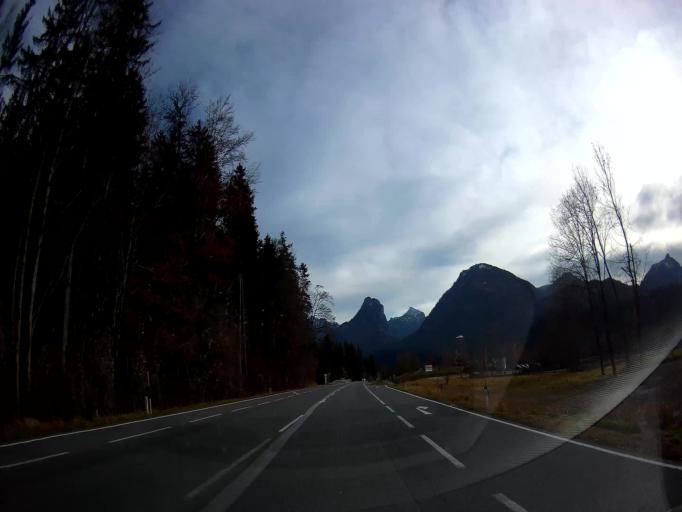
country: AT
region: Upper Austria
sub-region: Politischer Bezirk Gmunden
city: Sankt Wolfgang im Salzkammergut
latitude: 47.7322
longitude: 13.4153
